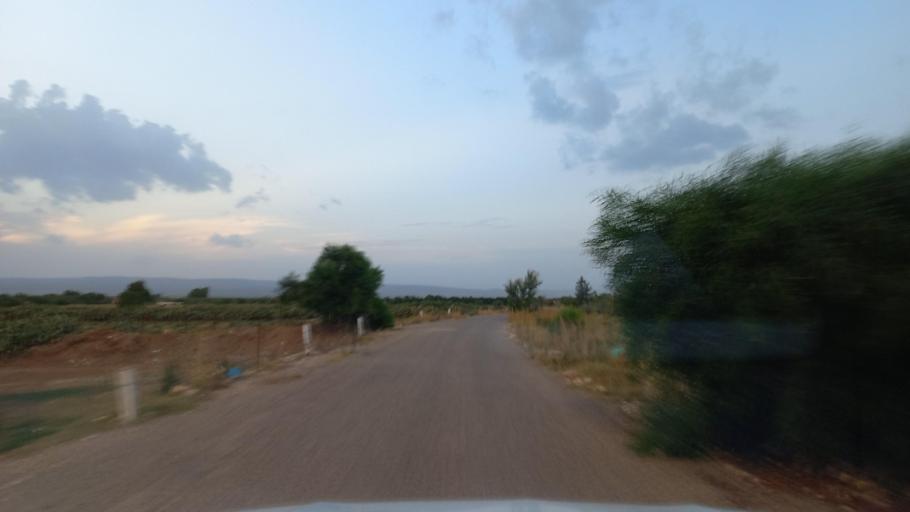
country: TN
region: Al Qasrayn
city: Kasserine
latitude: 35.2698
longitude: 9.0471
